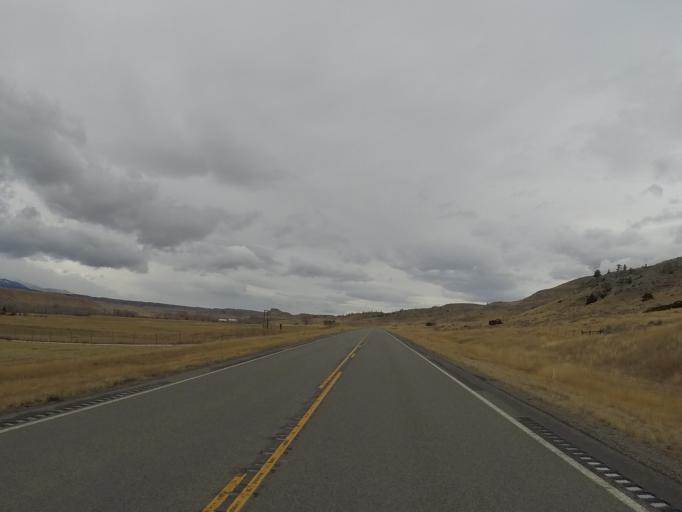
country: US
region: Montana
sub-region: Sweet Grass County
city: Big Timber
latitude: 45.9157
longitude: -109.9782
